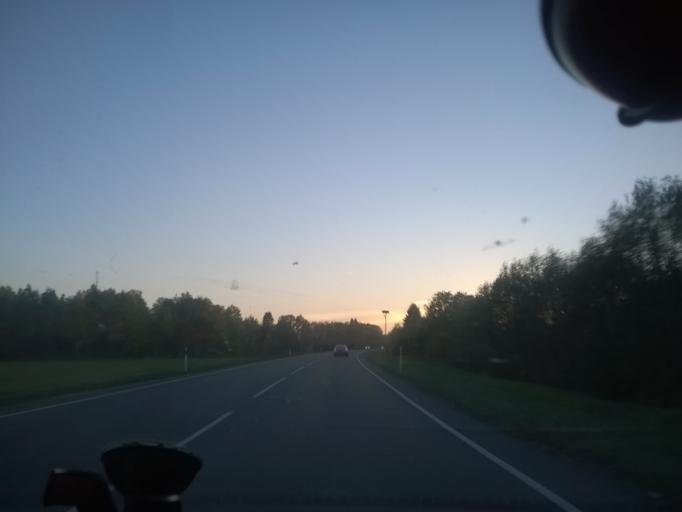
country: EE
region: Laeaene
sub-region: Ridala Parish
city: Uuemoisa
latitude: 58.9604
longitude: 23.8185
